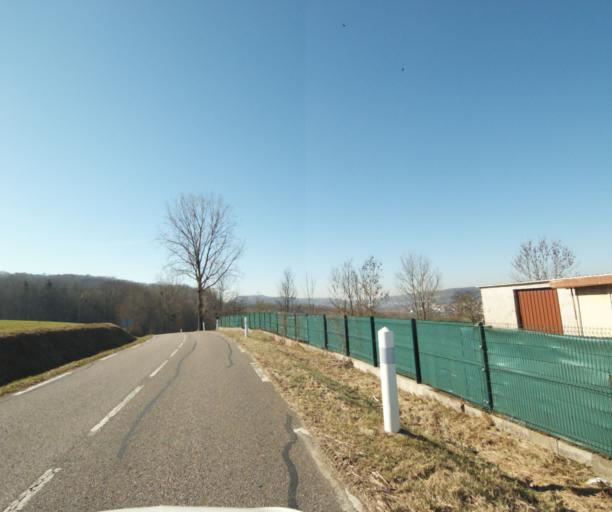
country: FR
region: Lorraine
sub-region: Departement de Meurthe-et-Moselle
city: Lay-Saint-Christophe
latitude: 48.7398
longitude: 6.1898
